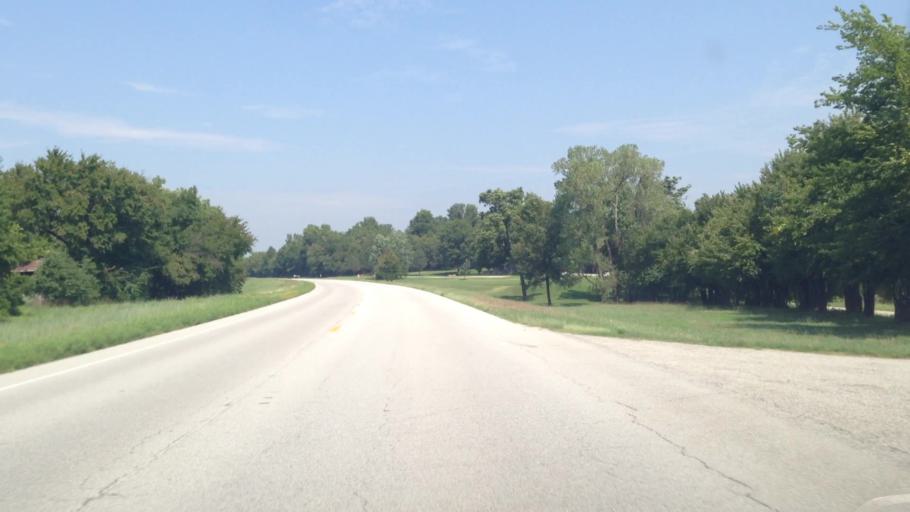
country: US
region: Kansas
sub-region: Labette County
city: Oswego
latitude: 37.1466
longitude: -95.1038
